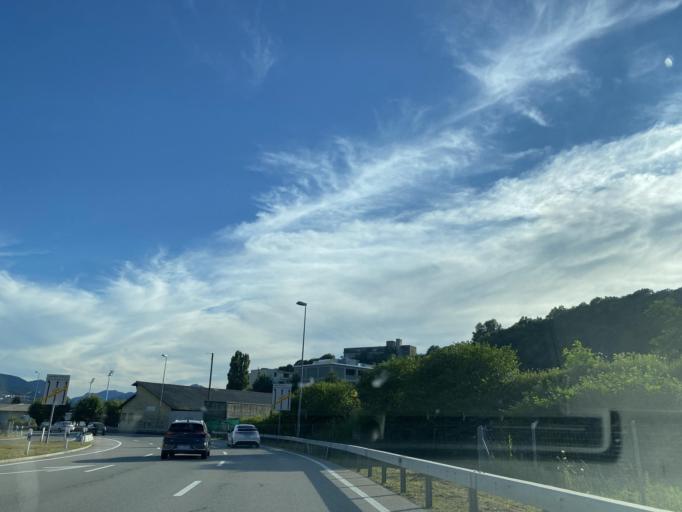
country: CH
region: Ticino
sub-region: Lugano District
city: Canobbio
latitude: 46.0287
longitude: 8.9661
